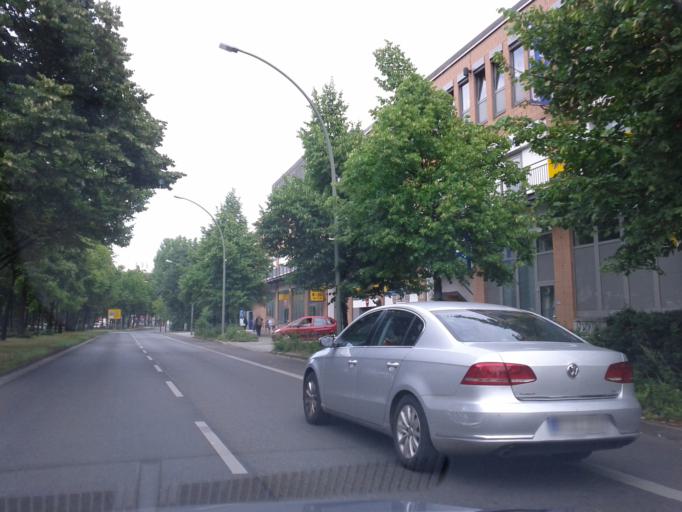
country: DE
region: Berlin
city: Prenzlauer Berg Bezirk
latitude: 52.5435
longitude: 13.4416
